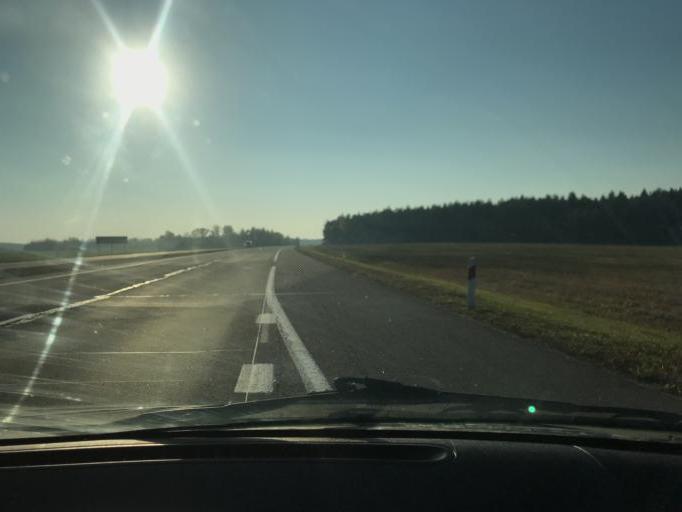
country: BY
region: Minsk
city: Krupki
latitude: 54.3175
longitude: 29.0525
